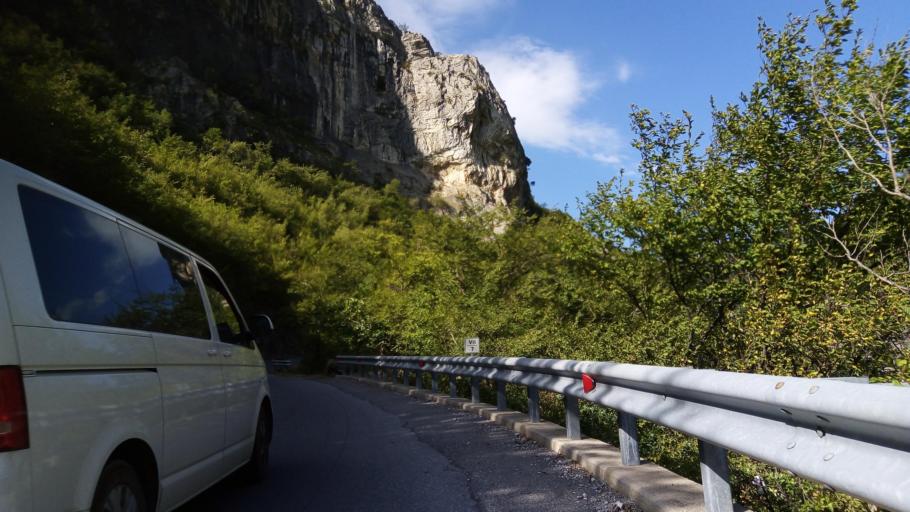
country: IT
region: Liguria
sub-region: Provincia di Savona
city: Balestrino
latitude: 44.1399
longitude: 8.1725
